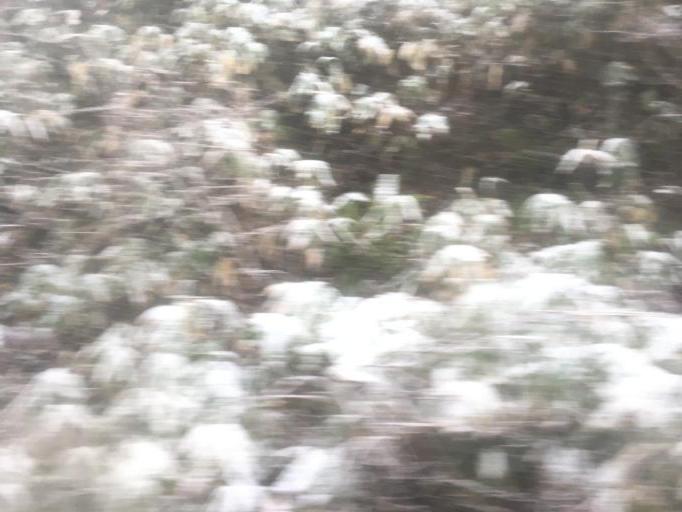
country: JP
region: Aomori
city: Goshogawara
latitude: 41.0984
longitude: 140.5284
